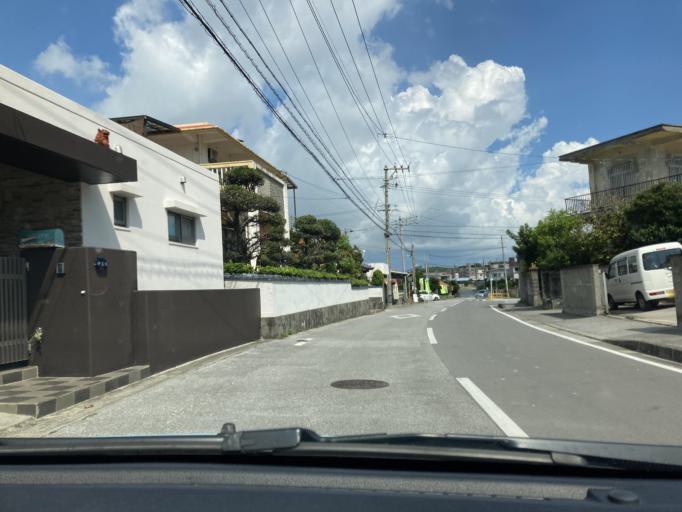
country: JP
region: Okinawa
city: Tomigusuku
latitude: 26.1523
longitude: 127.7544
